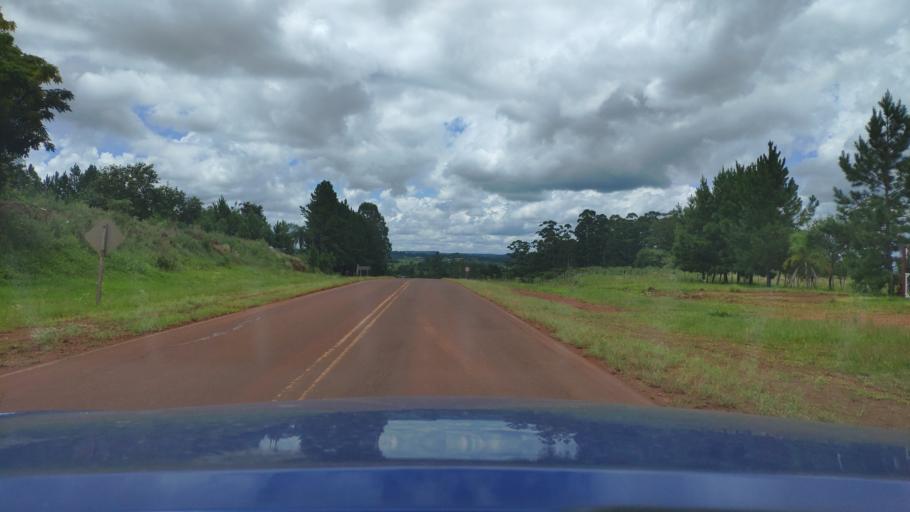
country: AR
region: Misiones
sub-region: Departamento de San Javier
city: San Javier
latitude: -27.8551
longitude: -55.2502
